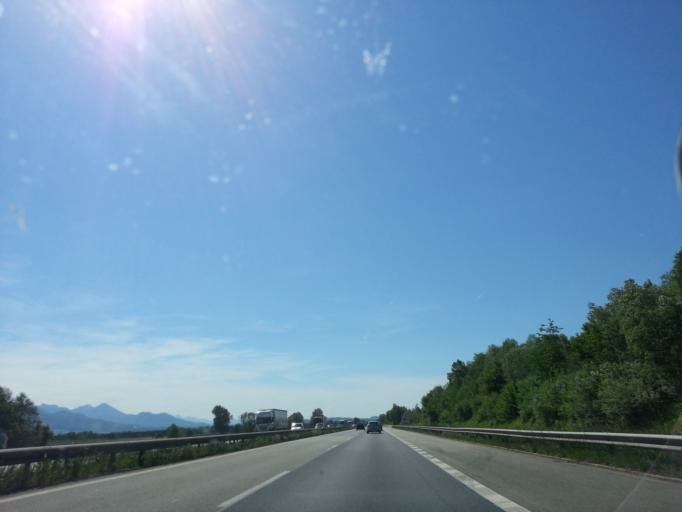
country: DE
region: Bavaria
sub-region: Upper Bavaria
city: Ubersee
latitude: 47.8386
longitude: 12.4699
